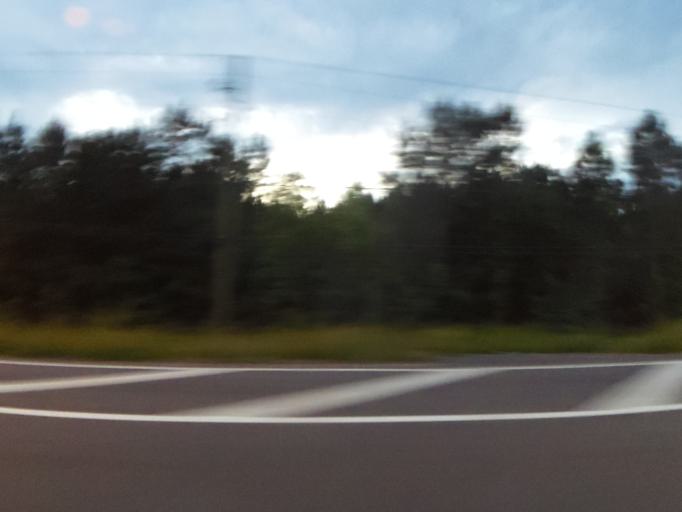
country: US
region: Georgia
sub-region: McDuffie County
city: Thomson
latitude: 33.5273
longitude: -82.5054
